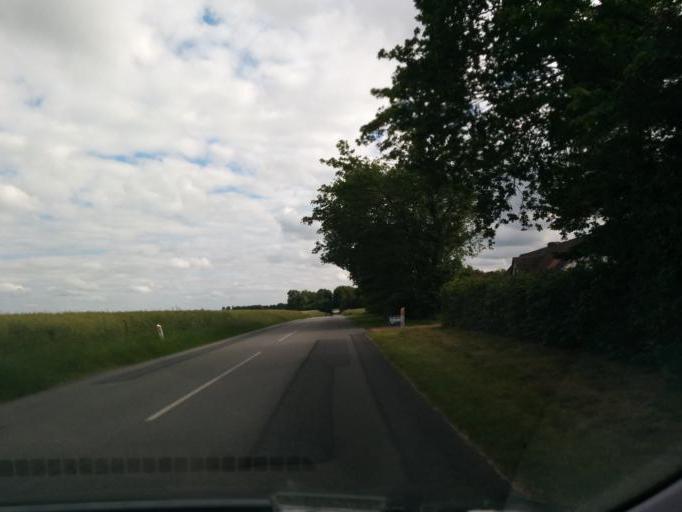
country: DK
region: Central Jutland
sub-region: Norddjurs Kommune
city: Grenaa
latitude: 56.4477
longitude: 10.7112
